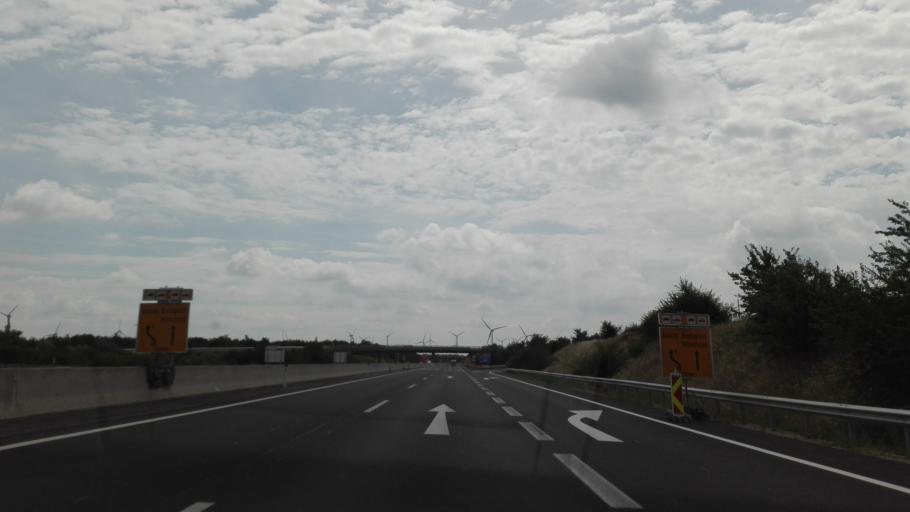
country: AT
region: Burgenland
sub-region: Politischer Bezirk Neusiedl am See
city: Gols
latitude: 47.9491
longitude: 16.9304
